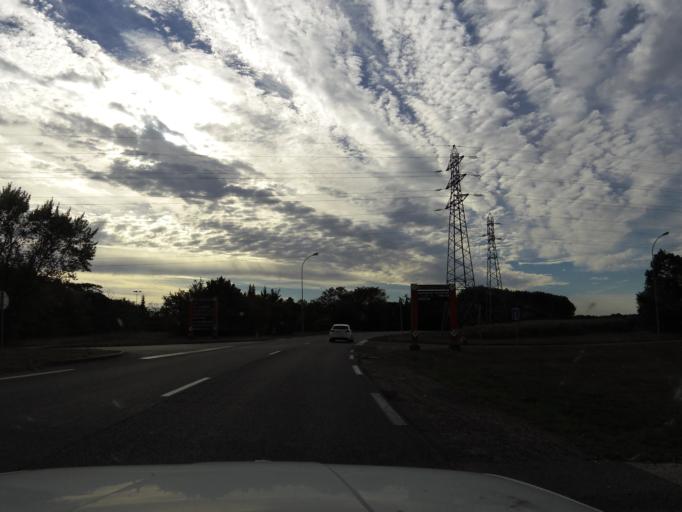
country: FR
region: Rhone-Alpes
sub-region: Departement de l'Ain
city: Saint-Jean-de-Niost
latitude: 45.8405
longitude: 5.2665
